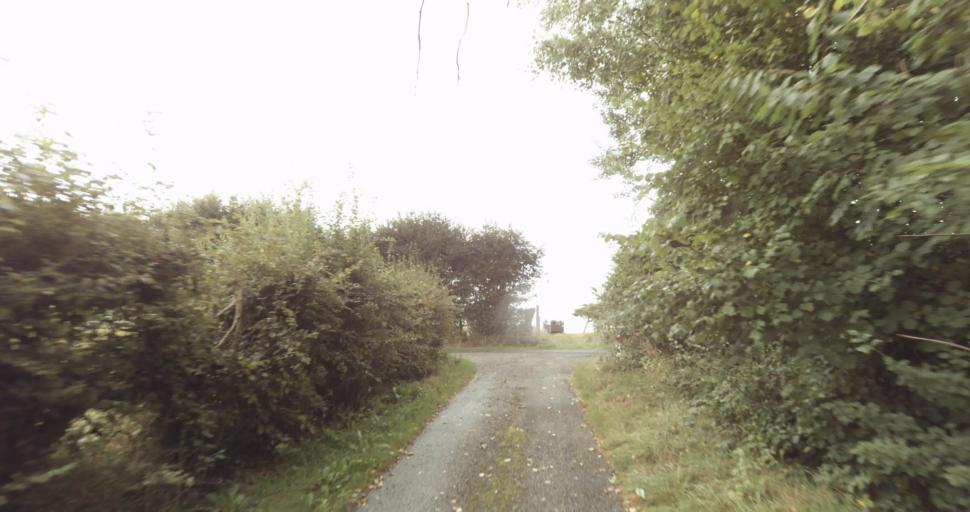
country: FR
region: Lower Normandy
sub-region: Departement de l'Orne
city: Vimoutiers
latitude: 48.8772
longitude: 0.1990
